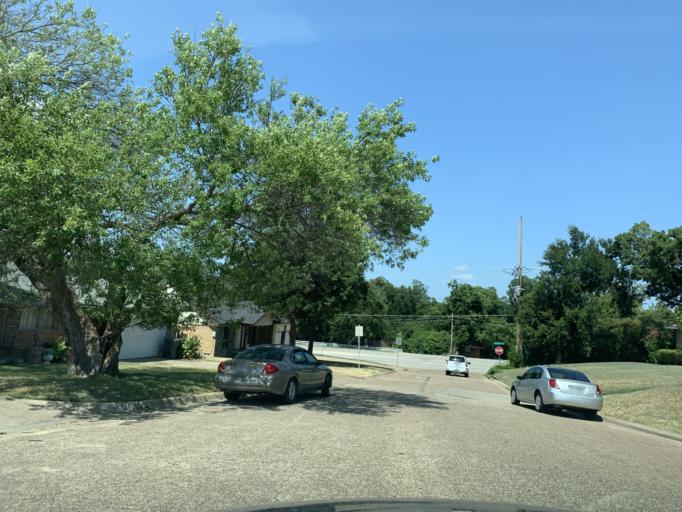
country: US
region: Texas
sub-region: Dallas County
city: Cockrell Hill
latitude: 32.6824
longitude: -96.8089
